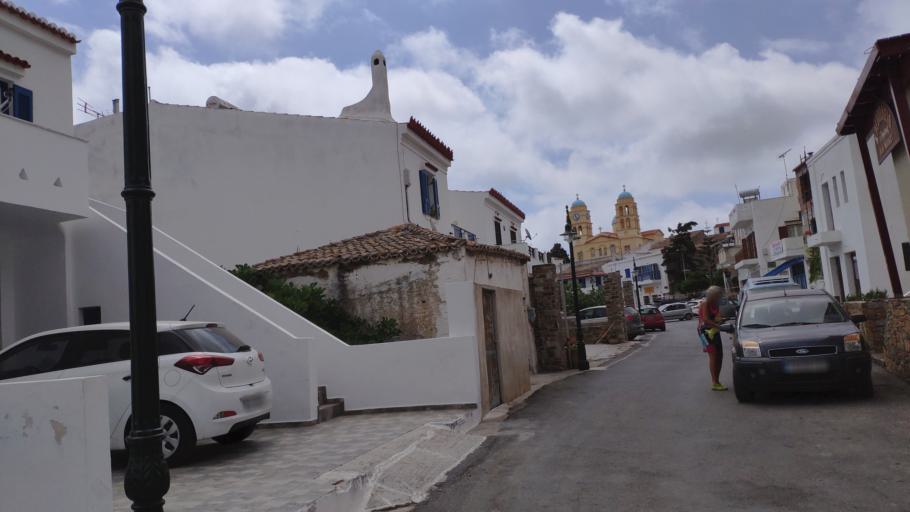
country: GR
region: South Aegean
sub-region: Nomos Kykladon
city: Kythnos
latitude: 37.3838
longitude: 24.4299
